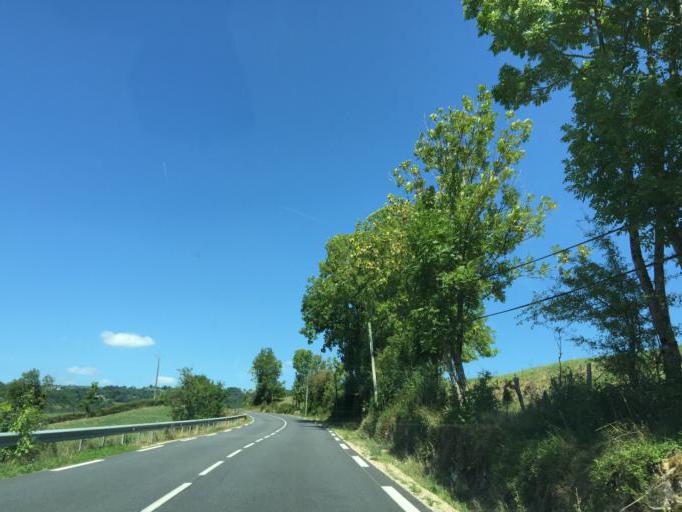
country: FR
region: Midi-Pyrenees
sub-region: Departement de l'Aveyron
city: Espalion
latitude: 44.5333
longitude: 2.7689
